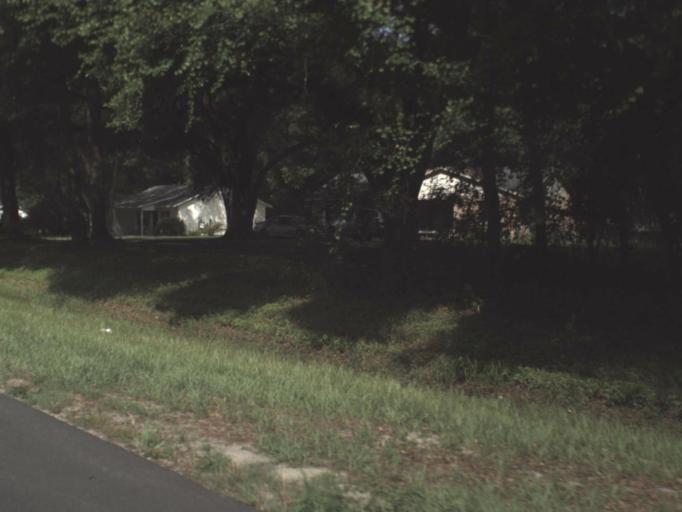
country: US
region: Florida
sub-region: Suwannee County
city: Live Oak
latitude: 30.2669
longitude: -83.0230
